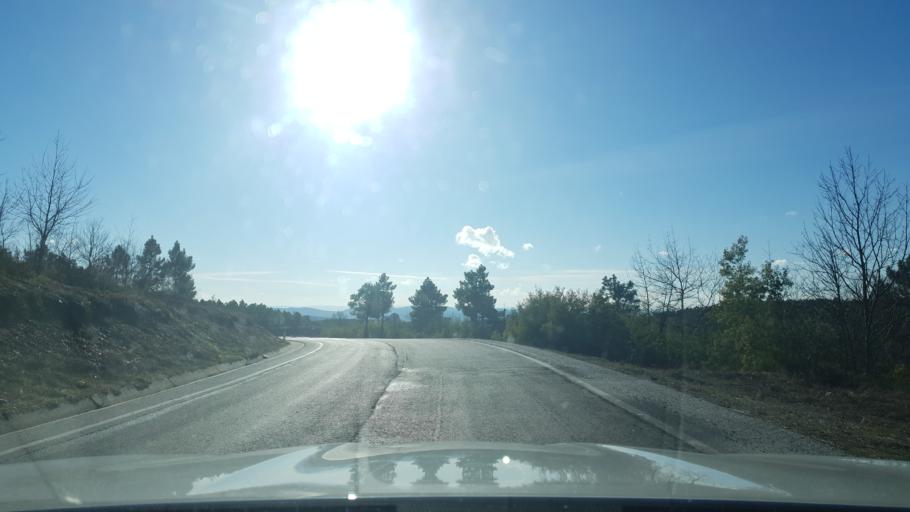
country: PT
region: Braganca
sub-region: Freixo de Espada A Cinta
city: Freixo de Espada a Cinta
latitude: 41.1366
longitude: -6.8075
